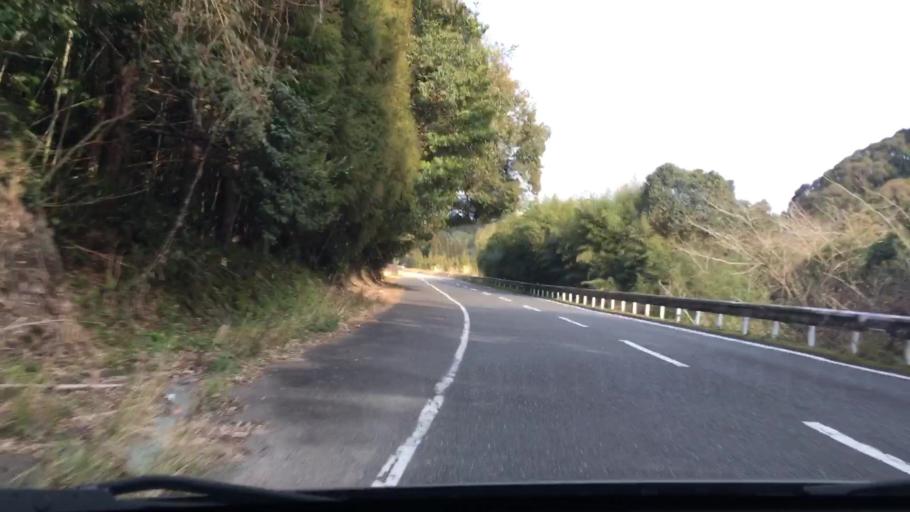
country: JP
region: Miyazaki
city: Nichinan
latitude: 31.5907
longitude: 131.3054
